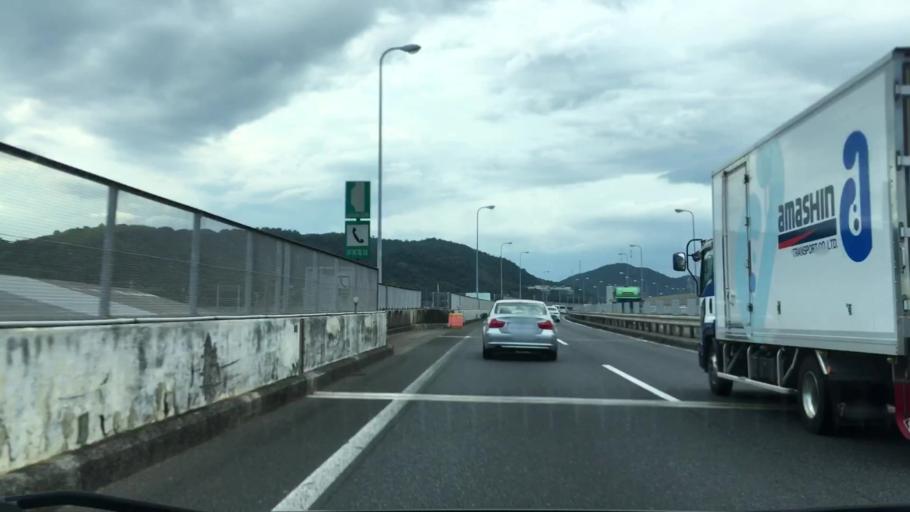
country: JP
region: Hyogo
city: Shirahamacho-usazakiminami
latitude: 34.7881
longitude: 134.7730
